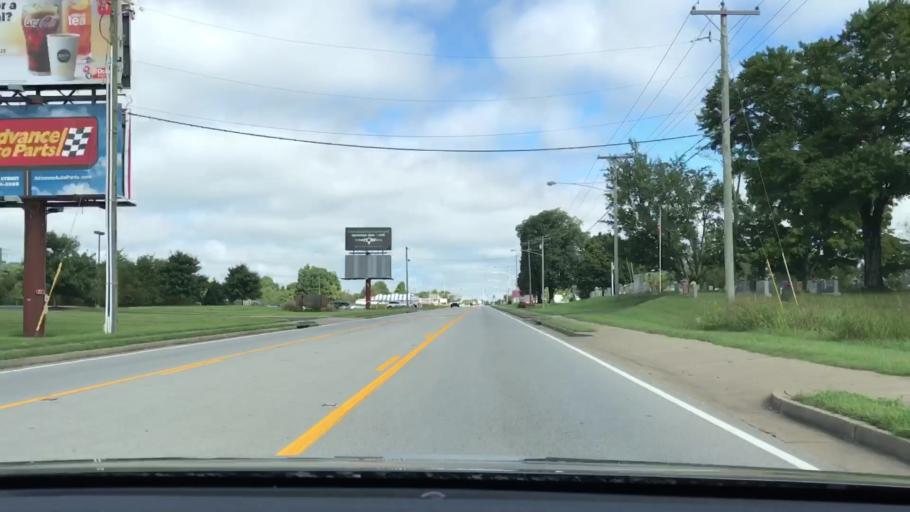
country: US
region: Kentucky
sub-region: Russell County
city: Jamestown
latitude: 37.0168
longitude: -85.0759
